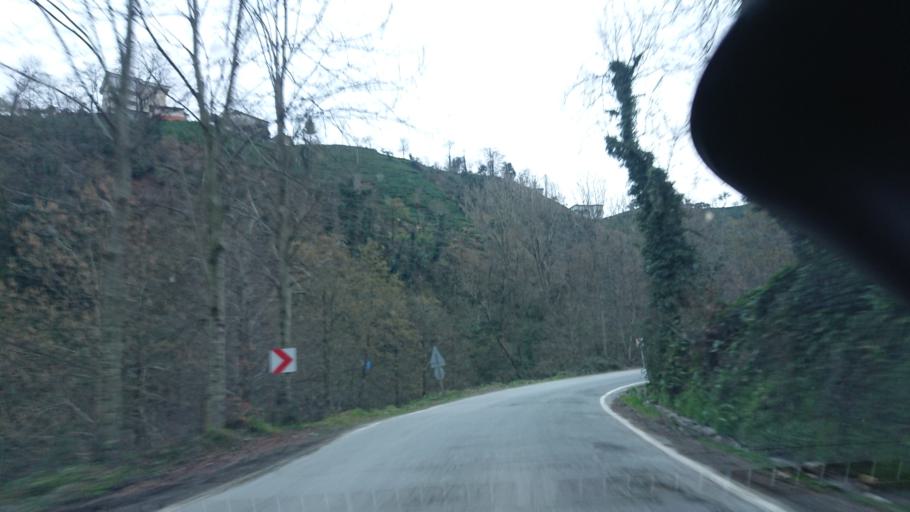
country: TR
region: Rize
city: Rize
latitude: 41.0226
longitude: 40.5025
